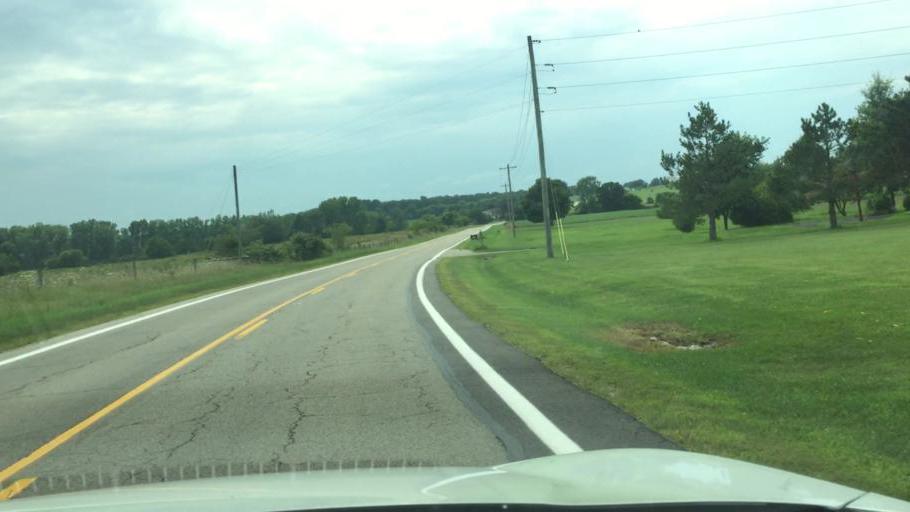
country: US
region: Ohio
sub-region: Champaign County
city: Mechanicsburg
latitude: 40.1006
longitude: -83.5452
